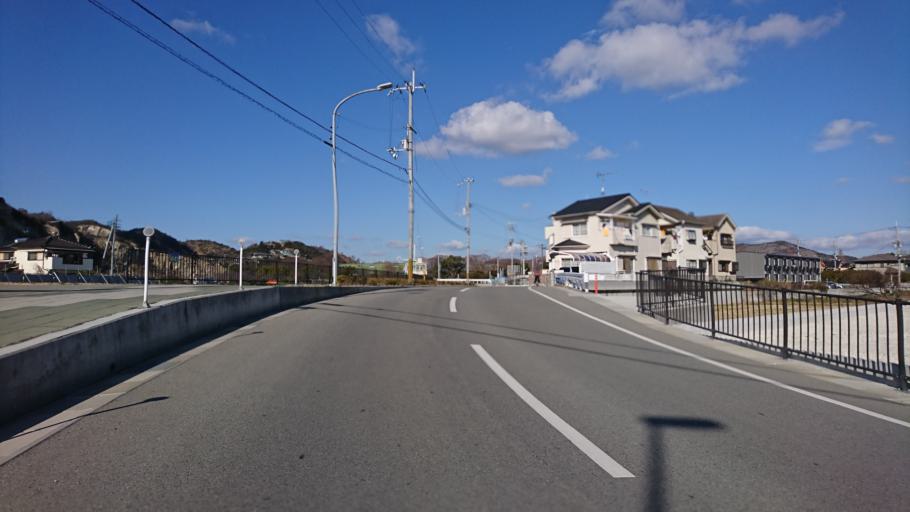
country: JP
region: Hyogo
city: Kakogawacho-honmachi
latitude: 34.7778
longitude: 134.8008
